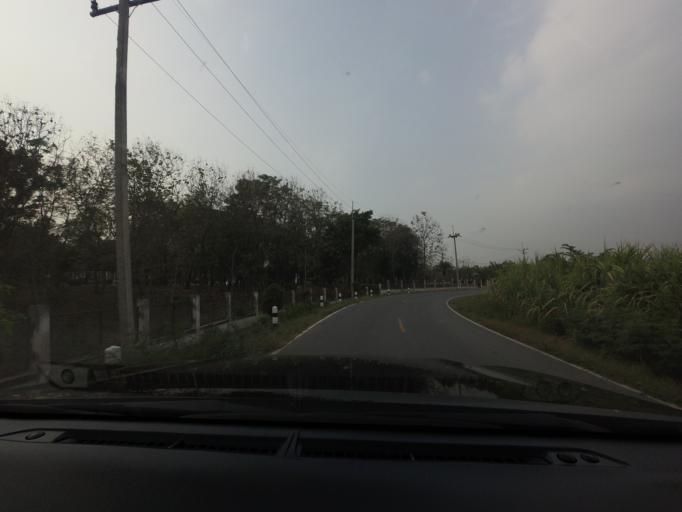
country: TH
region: Sara Buri
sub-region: Amphoe Wang Muang
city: Wang Muang
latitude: 14.8462
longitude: 101.1015
